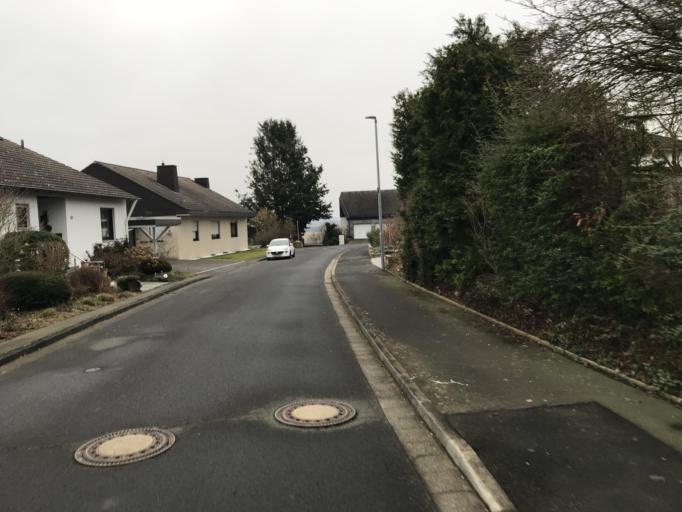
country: DE
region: Hesse
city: Fritzlar
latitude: 51.1305
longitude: 9.2647
